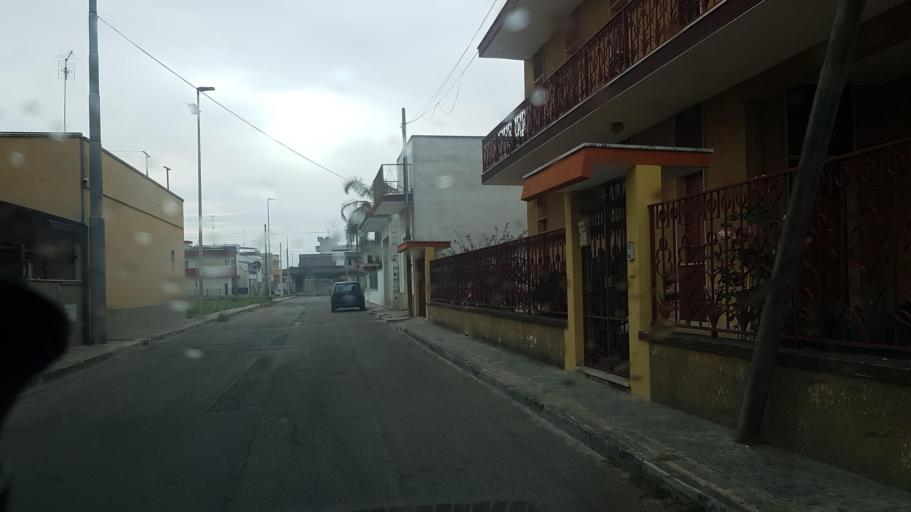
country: IT
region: Apulia
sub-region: Provincia di Lecce
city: Leverano
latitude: 40.2833
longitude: 17.9929
